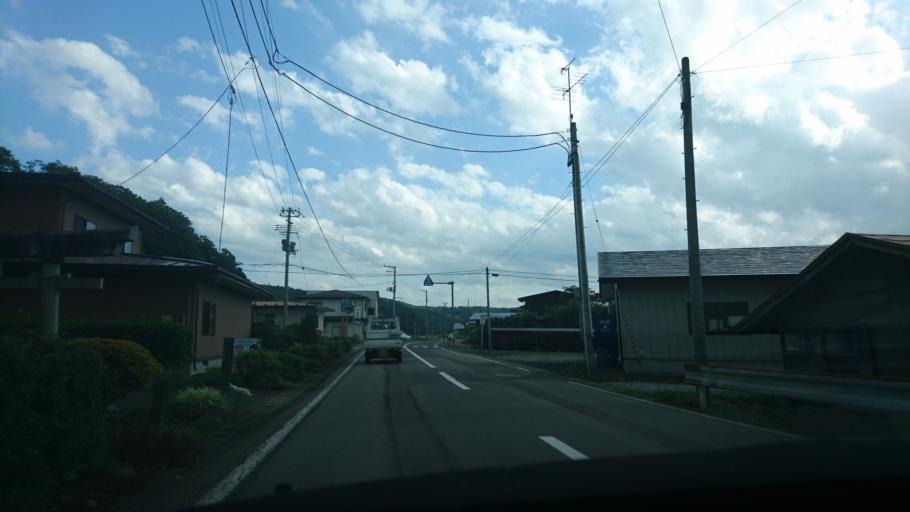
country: JP
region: Iwate
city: Kitakami
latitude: 39.3106
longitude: 141.1545
